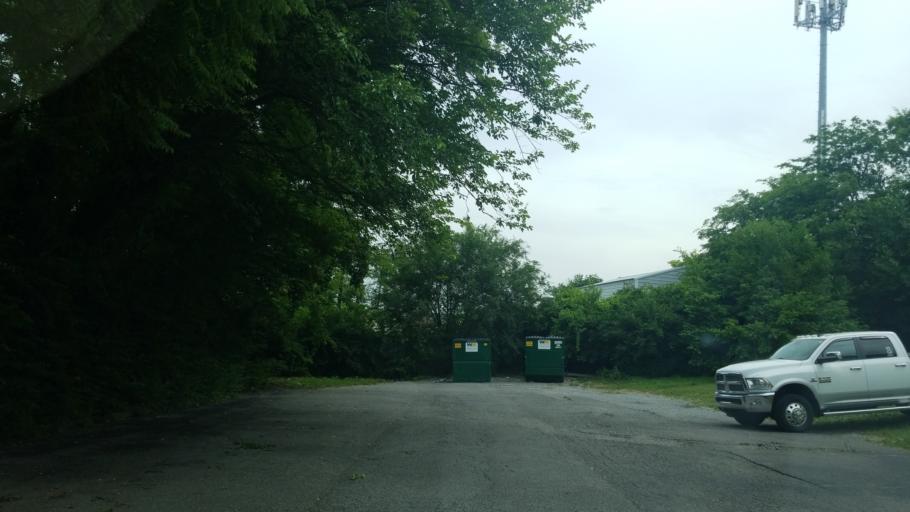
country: US
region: Tennessee
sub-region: Davidson County
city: Nashville
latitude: 36.1405
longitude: -86.7686
